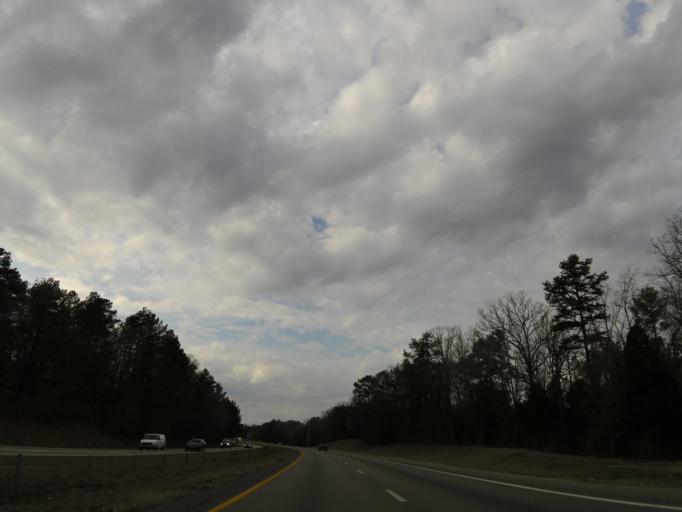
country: US
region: South Carolina
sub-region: Lexington County
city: Irmo
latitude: 34.1319
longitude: -81.2087
